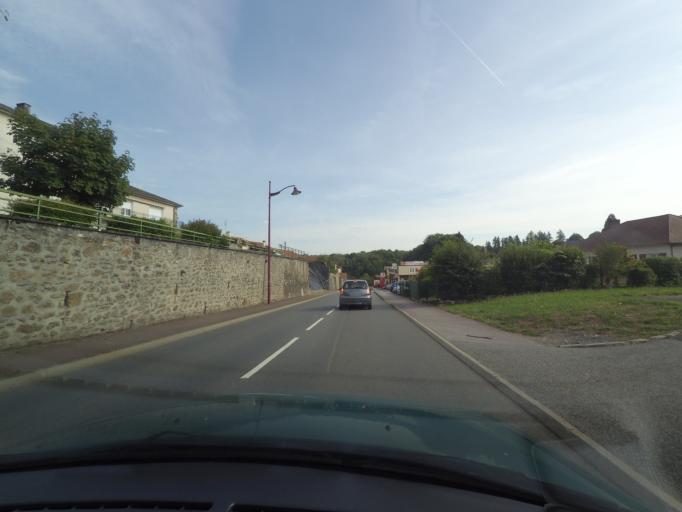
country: FR
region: Limousin
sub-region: Departement de la Haute-Vienne
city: Rochechouart
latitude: 45.8217
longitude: 0.8255
